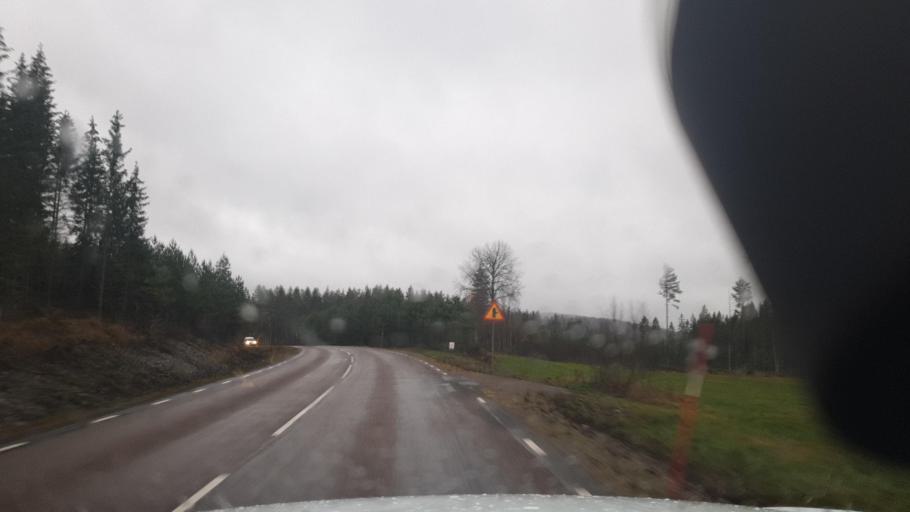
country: SE
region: Vaermland
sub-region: Eda Kommun
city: Amotfors
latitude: 59.7325
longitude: 12.1704
